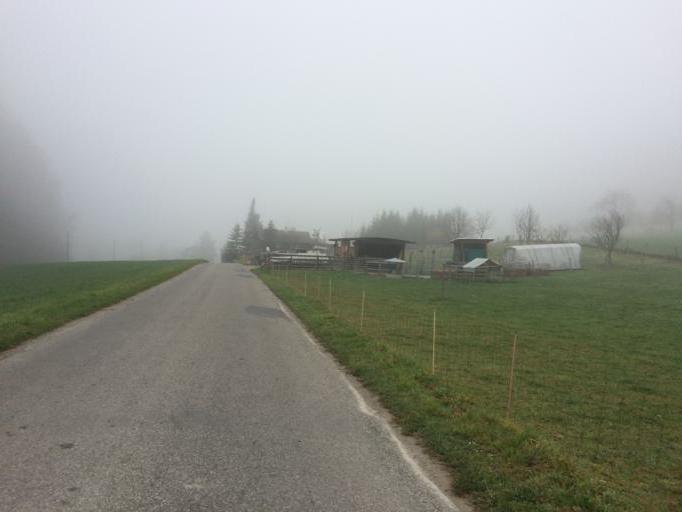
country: CH
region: Bern
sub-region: Bern-Mittelland District
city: Koniz
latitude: 46.9103
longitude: 7.4408
